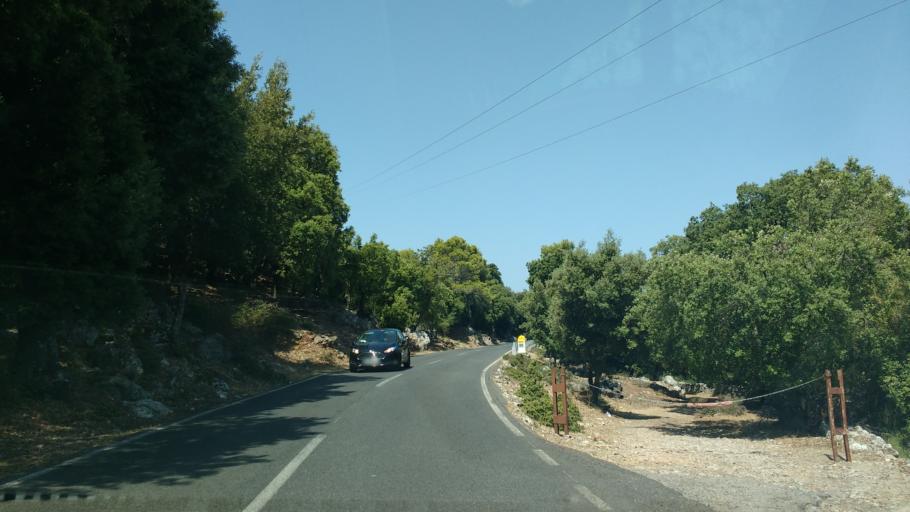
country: ES
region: Balearic Islands
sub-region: Illes Balears
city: Escorca
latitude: 39.8250
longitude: 2.8497
